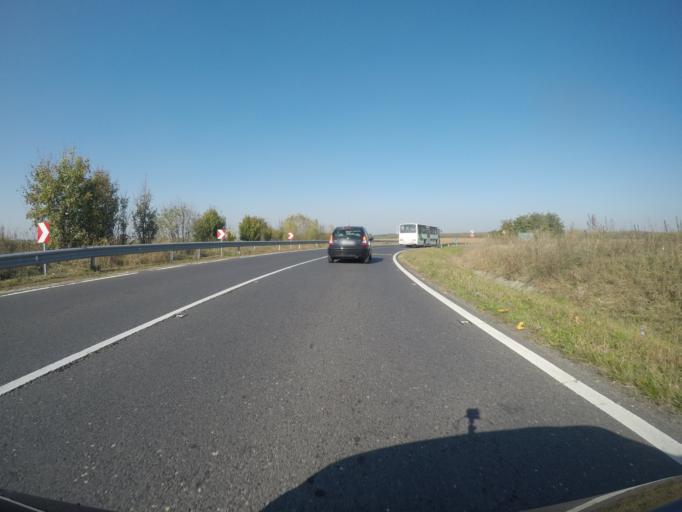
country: HU
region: Tolna
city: Szedres
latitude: 46.4962
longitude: 18.6732
